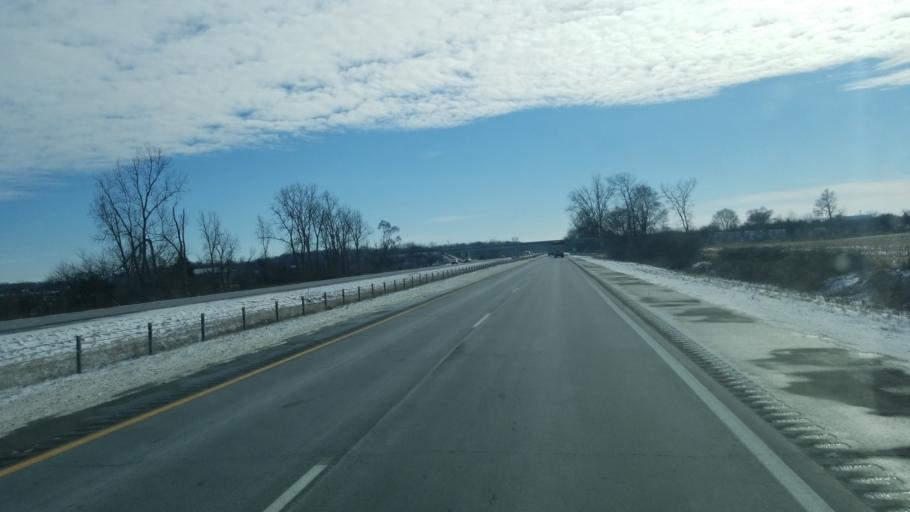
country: US
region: Michigan
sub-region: Washtenaw County
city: Milan
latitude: 42.0653
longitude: -83.6706
